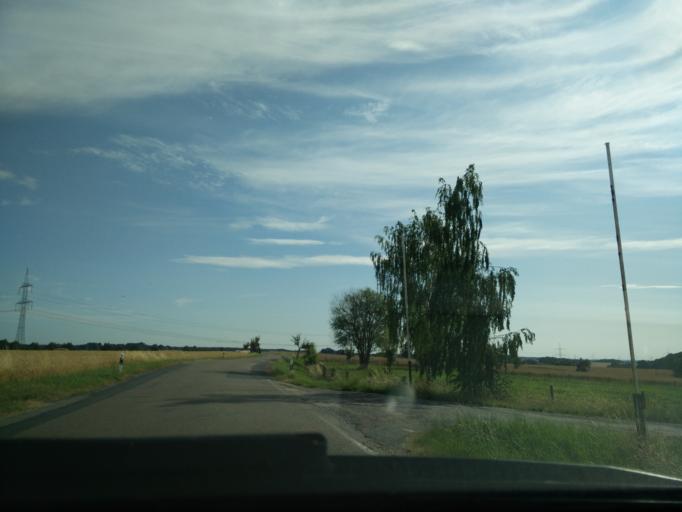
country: DE
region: Saxony
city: Geithain
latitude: 51.0983
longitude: 12.6950
